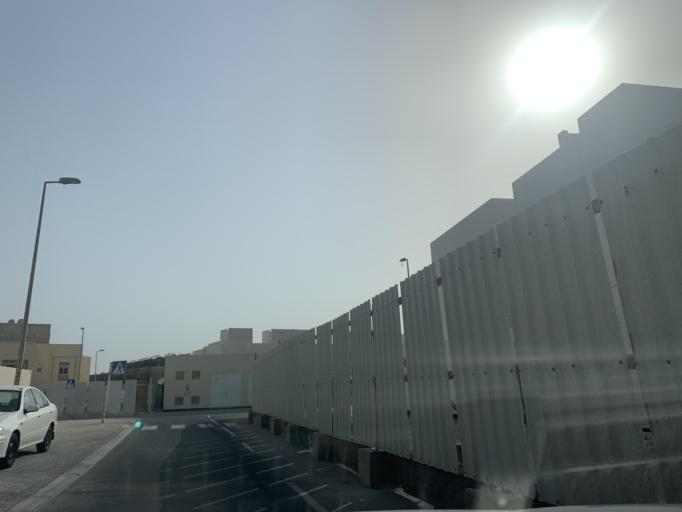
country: BH
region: Manama
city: Jidd Hafs
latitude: 26.2303
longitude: 50.4467
